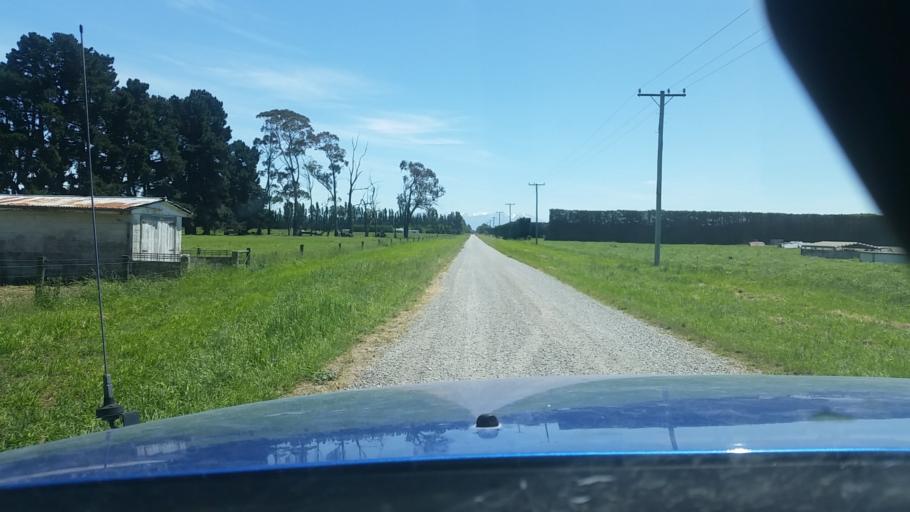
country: NZ
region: Canterbury
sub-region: Ashburton District
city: Tinwald
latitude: -43.9420
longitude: 171.7563
